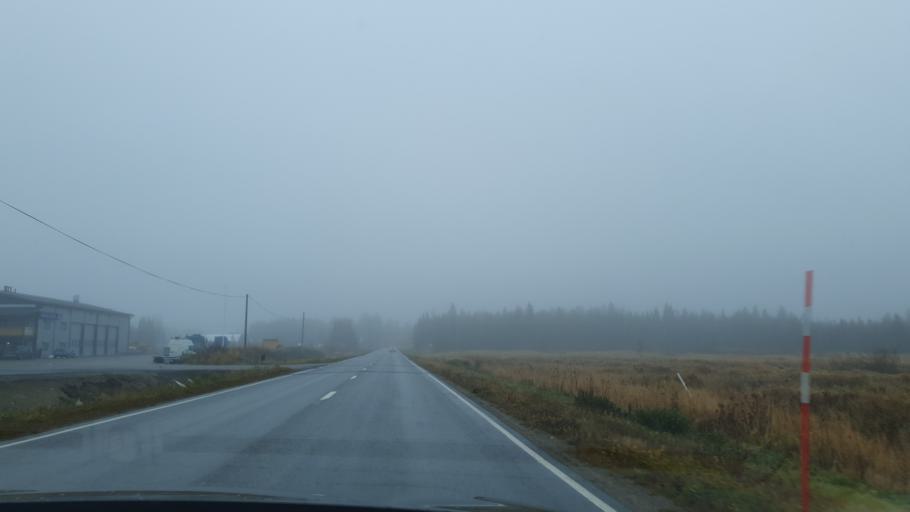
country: FI
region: Lapland
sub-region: Tunturi-Lappi
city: Kittilae
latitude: 67.6686
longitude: 24.8661
